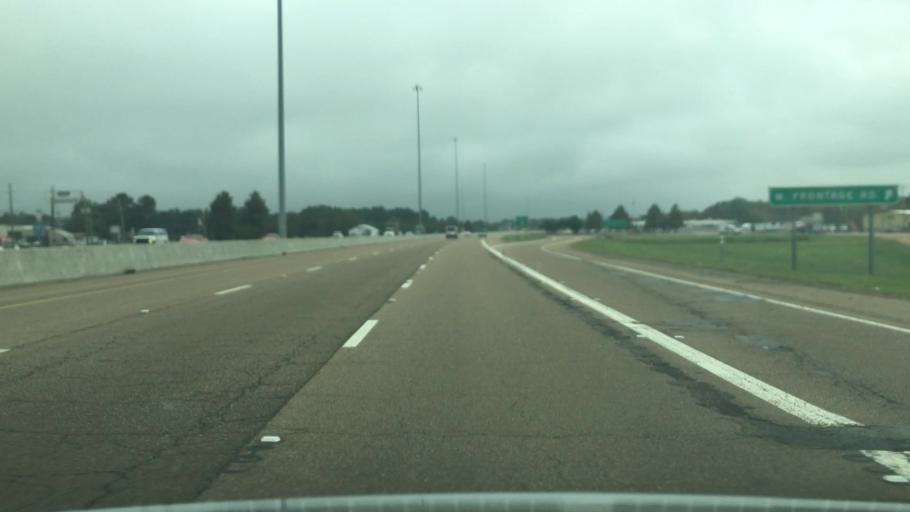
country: US
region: Mississippi
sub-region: Rankin County
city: Richland
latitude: 32.2559
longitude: -90.1613
